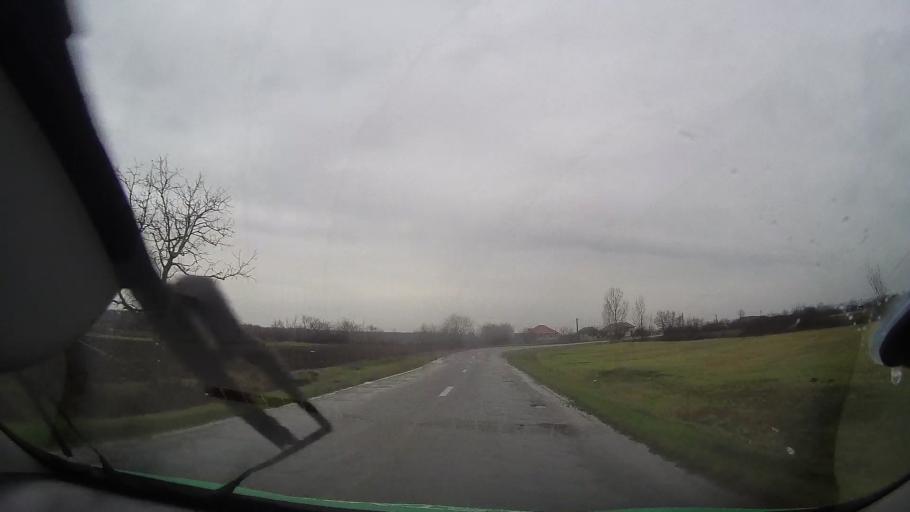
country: RO
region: Bihor
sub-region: Comuna Cociuba Mare
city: Cociuba Mare
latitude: 46.7387
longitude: 21.9891
